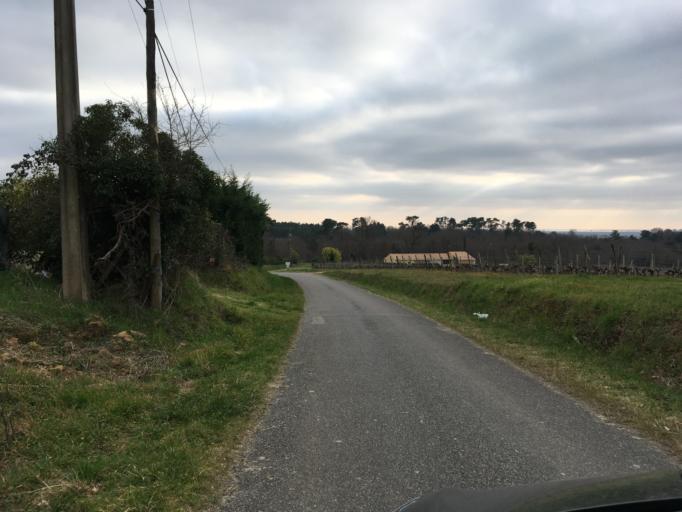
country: FR
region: Aquitaine
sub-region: Departement de la Gironde
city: Saint-Ciers-sur-Gironde
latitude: 45.3110
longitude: -0.6081
